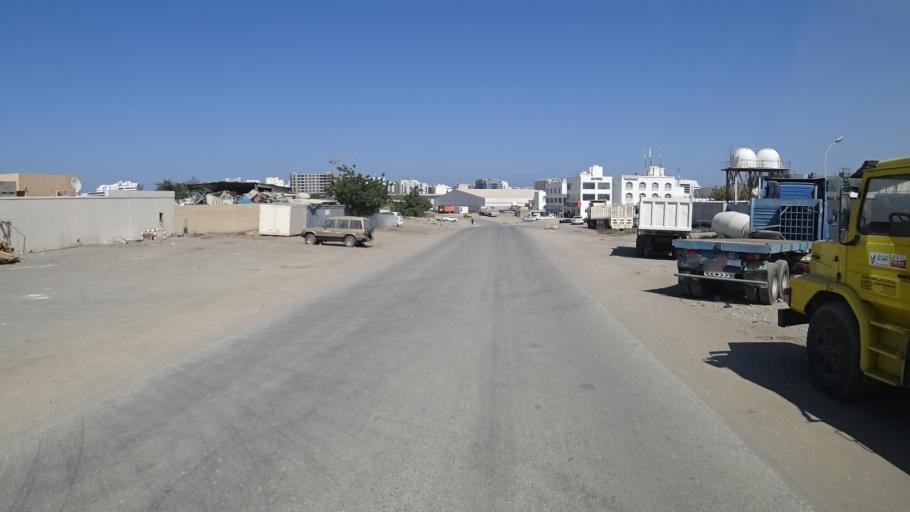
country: OM
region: Muhafazat Masqat
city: Bawshar
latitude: 23.5769
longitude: 58.3680
